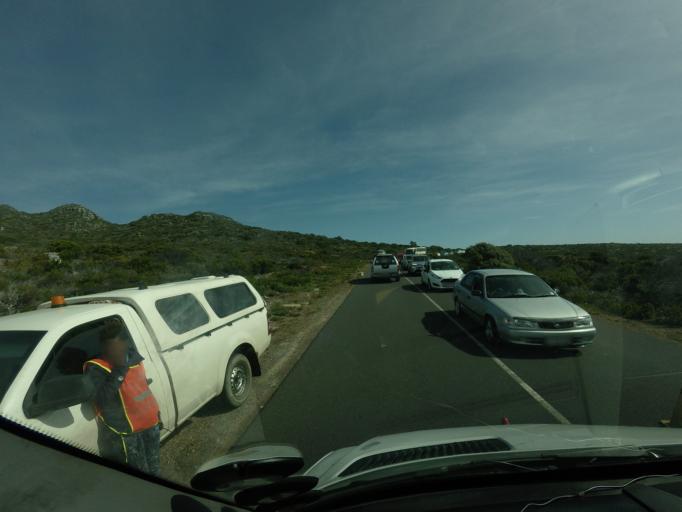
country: ZA
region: Western Cape
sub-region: City of Cape Town
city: Retreat
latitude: -34.3428
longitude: 18.4671
